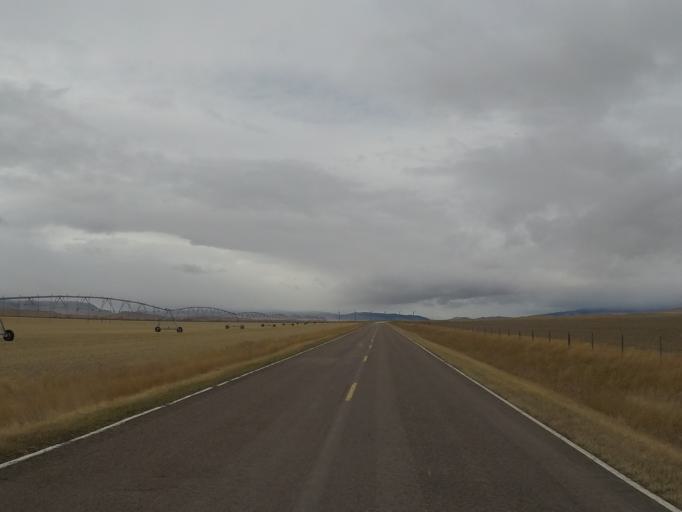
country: US
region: Montana
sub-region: Wheatland County
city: Harlowton
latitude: 46.4516
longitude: -110.1695
